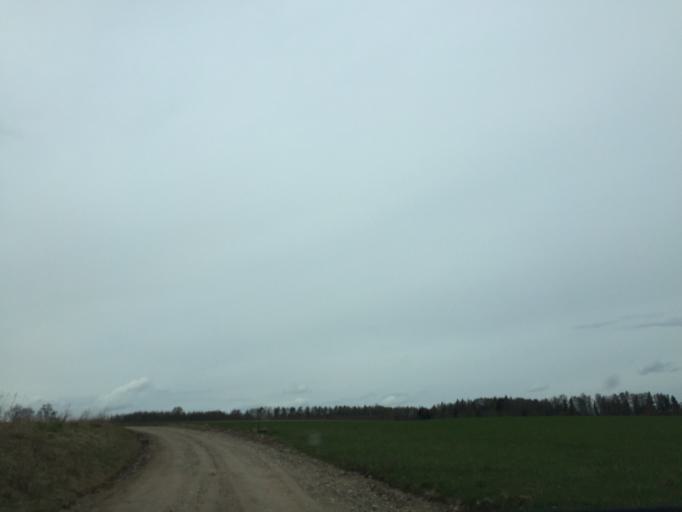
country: LV
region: Priekuli
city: Priekuli
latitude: 57.3327
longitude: 25.3839
